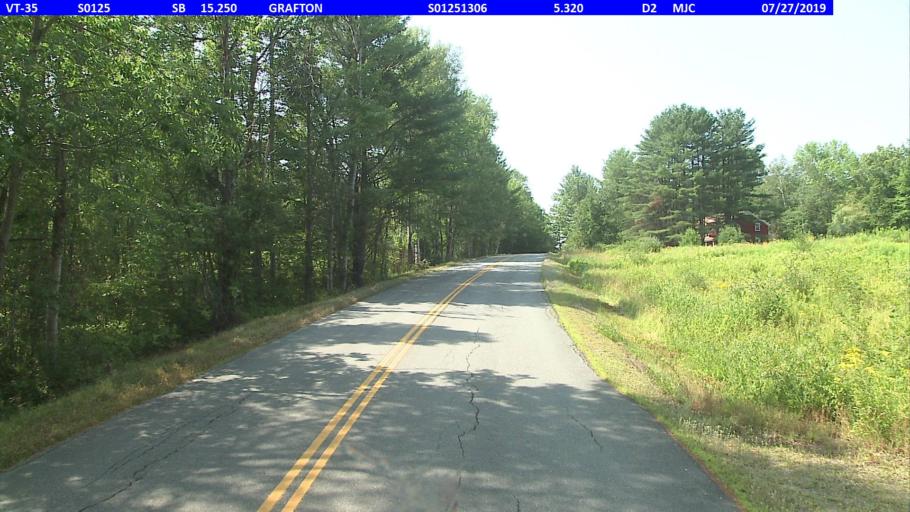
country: US
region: Vermont
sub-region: Windsor County
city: Chester
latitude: 43.1874
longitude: -72.5980
